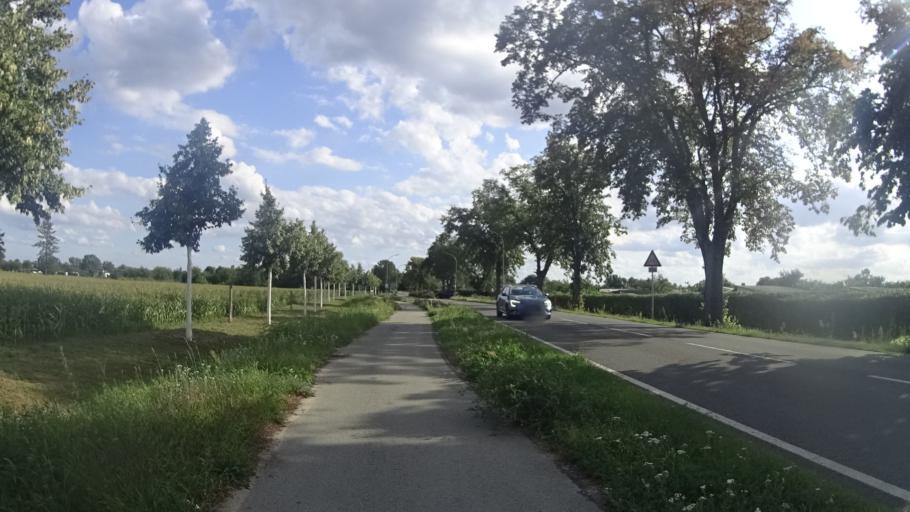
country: DE
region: Brandenburg
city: Rathenow
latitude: 52.6234
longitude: 12.3310
